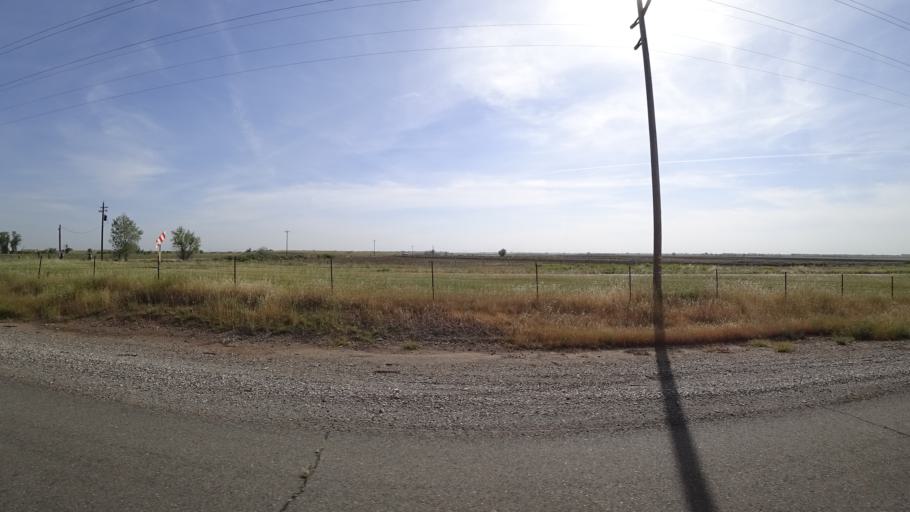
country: US
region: California
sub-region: Butte County
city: Durham
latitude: 39.6354
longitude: -121.7086
